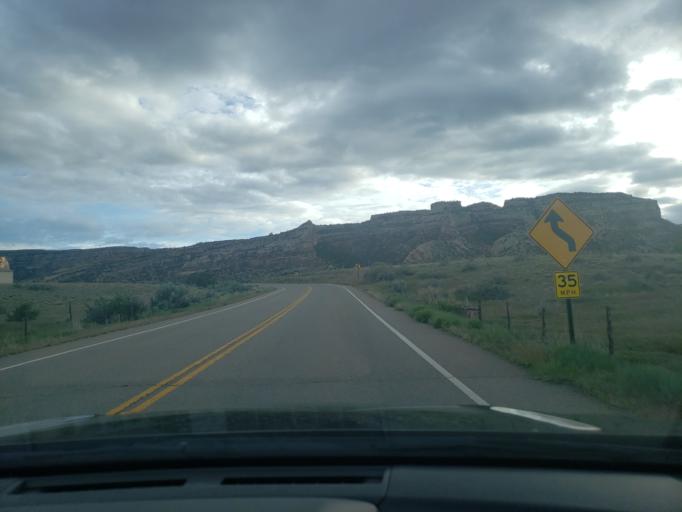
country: US
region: Colorado
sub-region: Mesa County
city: Redlands
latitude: 39.0420
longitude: -108.6272
